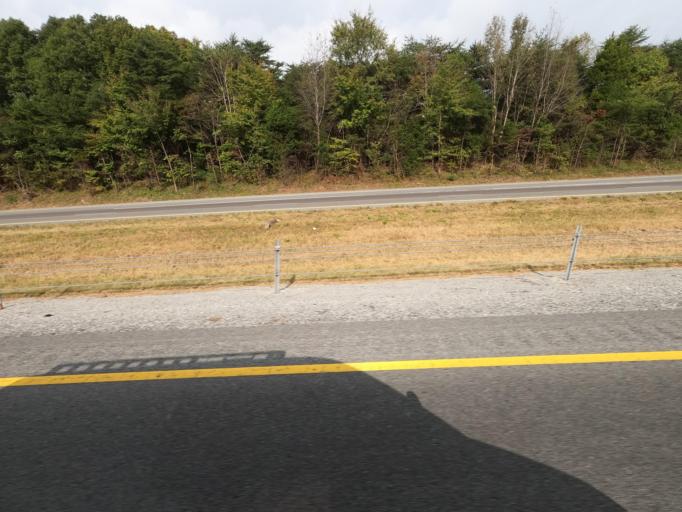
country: US
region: Tennessee
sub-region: Williamson County
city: Fairview
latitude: 36.0252
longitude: -87.1817
